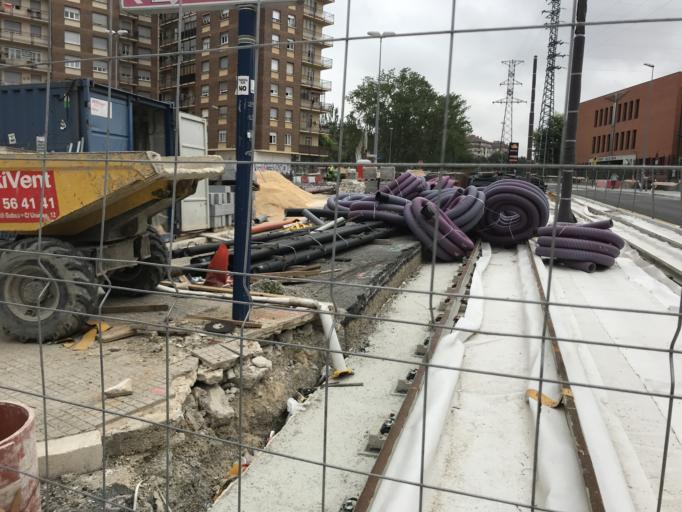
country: ES
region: Basque Country
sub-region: Provincia de Alava
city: Gasteiz / Vitoria
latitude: 42.8395
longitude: -2.6645
